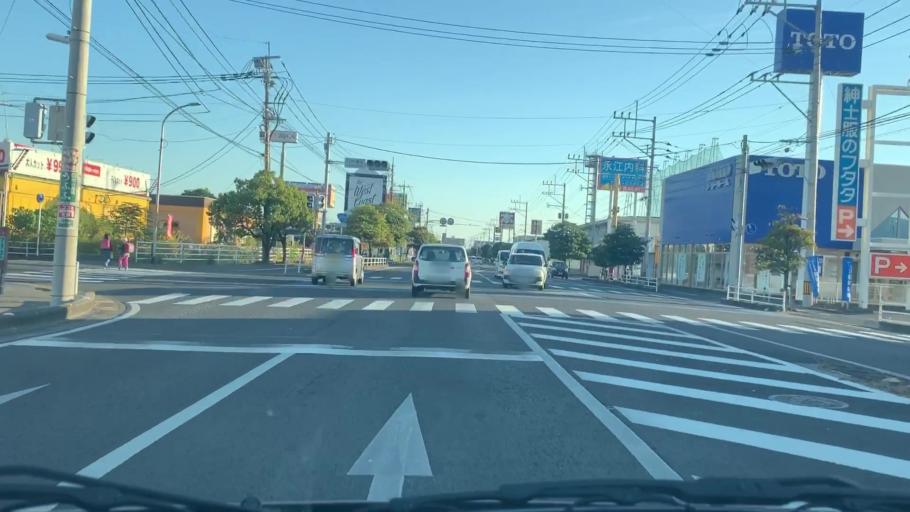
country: JP
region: Saga Prefecture
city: Saga-shi
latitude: 33.2675
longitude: 130.2717
